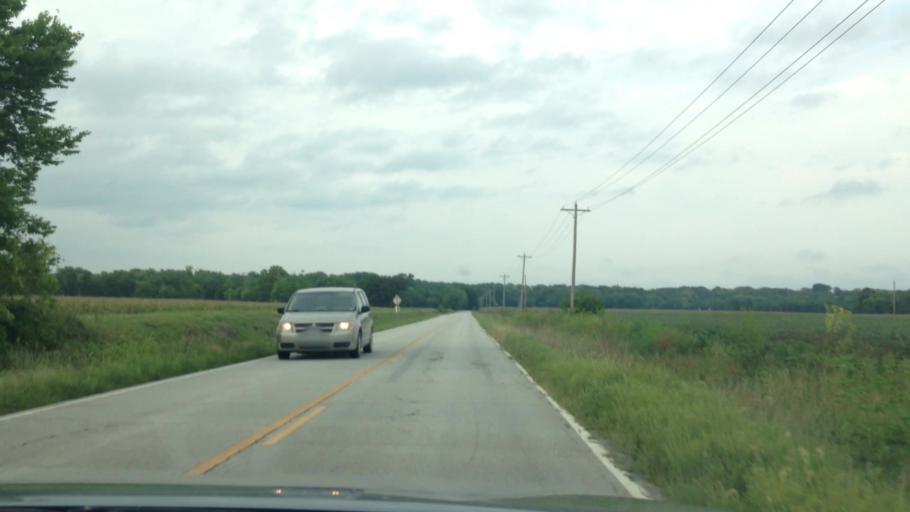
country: US
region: Missouri
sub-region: Clay County
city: Smithville
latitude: 39.3957
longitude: -94.6620
